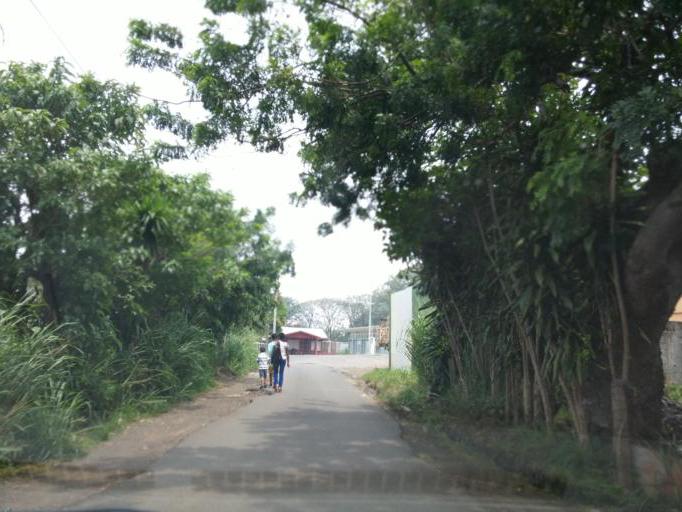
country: CR
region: Alajuela
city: Alajuela
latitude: 9.9927
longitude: -84.2058
